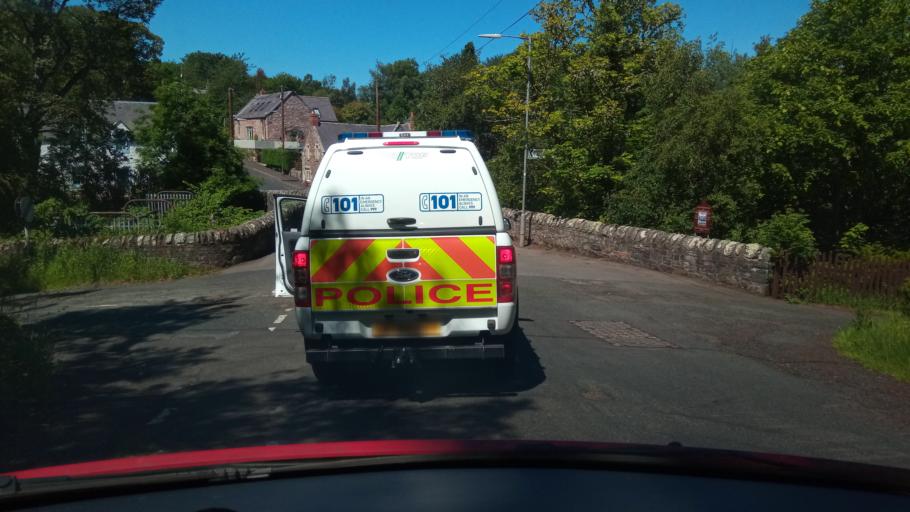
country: GB
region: Scotland
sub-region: The Scottish Borders
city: Duns
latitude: 55.8074
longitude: -2.4911
